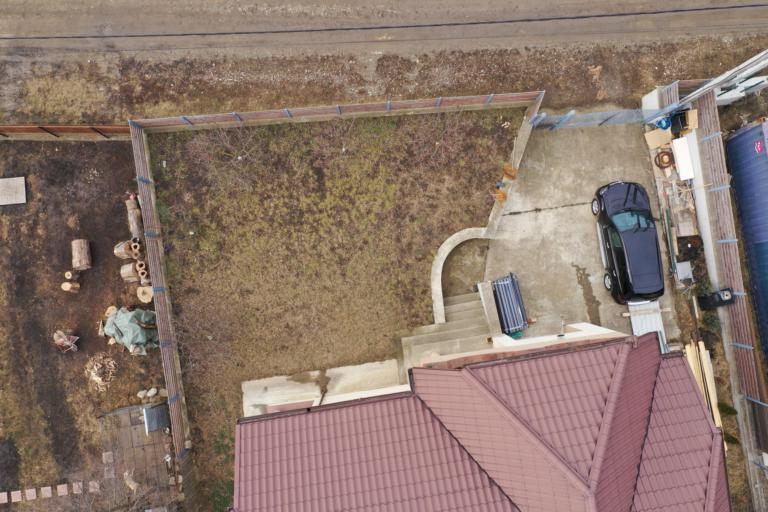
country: RO
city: Vanatori
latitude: 47.2521
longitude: 27.5225
